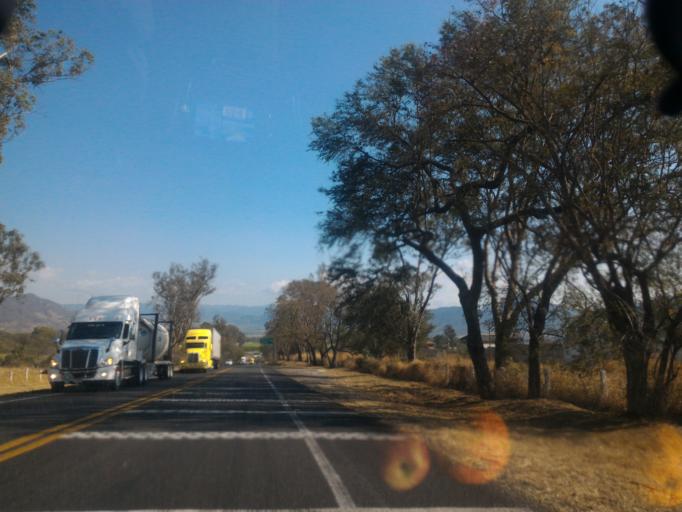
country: MX
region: Jalisco
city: Tuxpan
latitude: 19.5417
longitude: -103.4266
